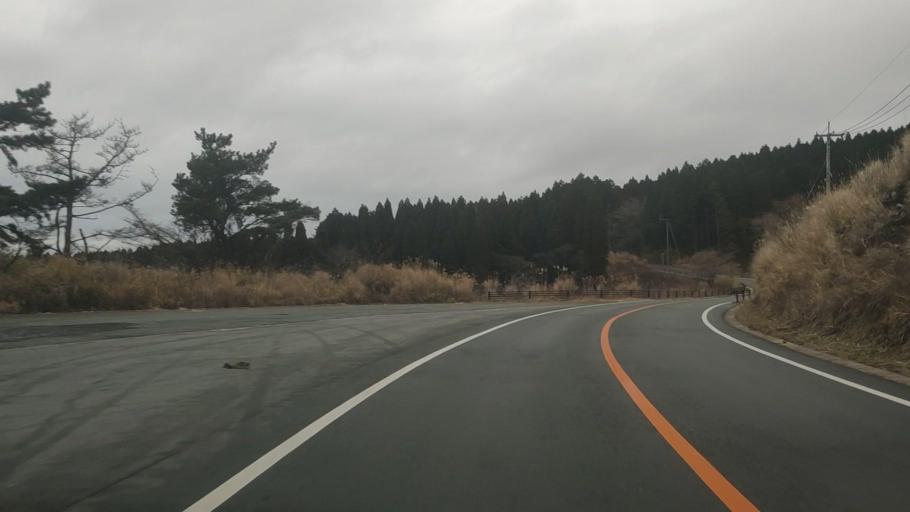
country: JP
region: Kumamoto
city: Aso
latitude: 32.8958
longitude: 131.0273
